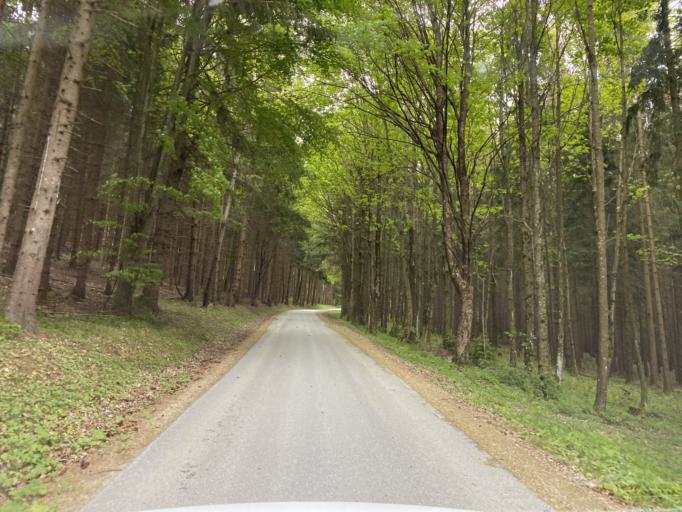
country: AT
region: Styria
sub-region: Politischer Bezirk Weiz
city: Koglhof
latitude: 47.3112
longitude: 15.7082
